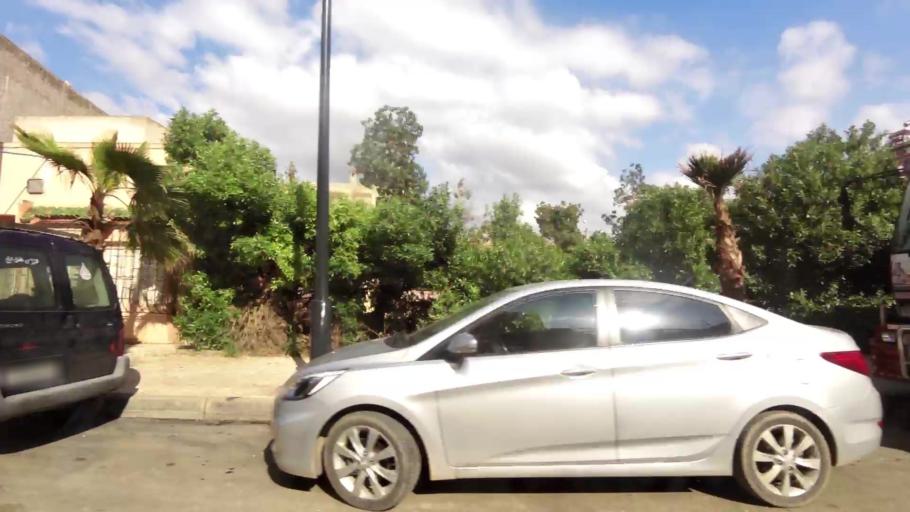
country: MA
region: Chaouia-Ouardigha
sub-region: Settat Province
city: Berrechid
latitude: 33.2613
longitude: -7.5716
